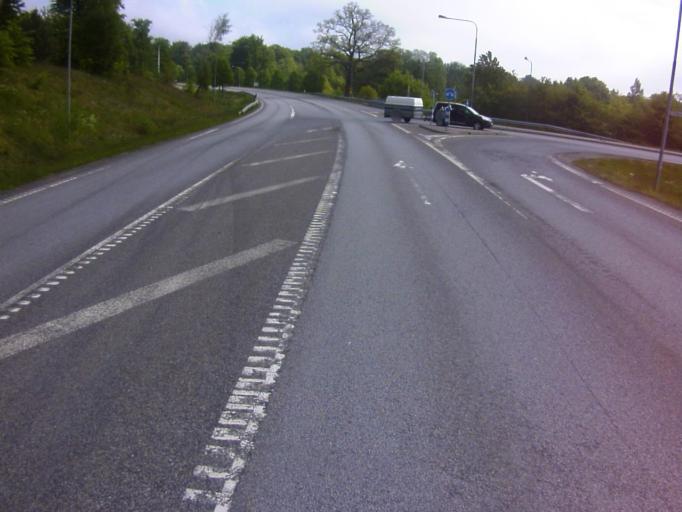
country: SE
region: Blekinge
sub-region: Solvesborgs Kommun
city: Soelvesborg
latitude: 56.0601
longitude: 14.5946
